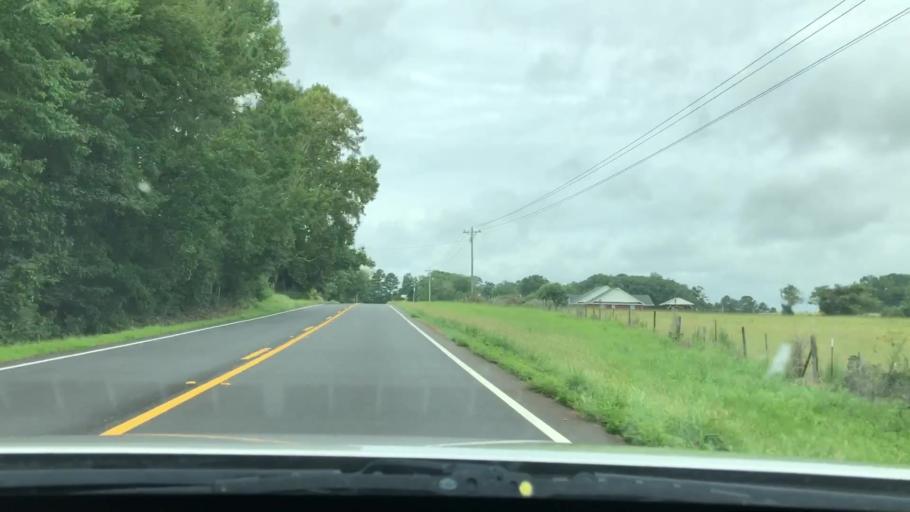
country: US
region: Georgia
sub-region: Upson County
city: Hannahs Mill
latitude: 33.0126
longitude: -84.4308
